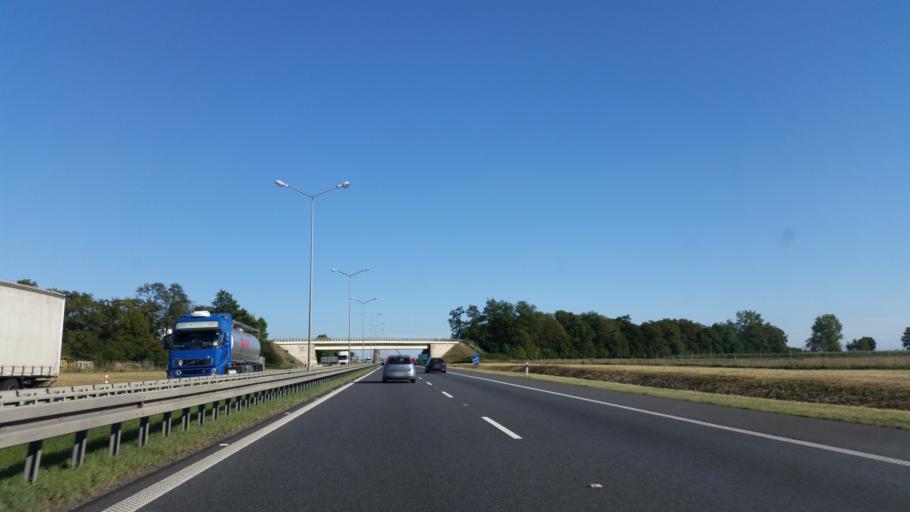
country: PL
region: Lower Silesian Voivodeship
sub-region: Powiat olawski
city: Wierzbno
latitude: 50.8840
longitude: 17.1956
